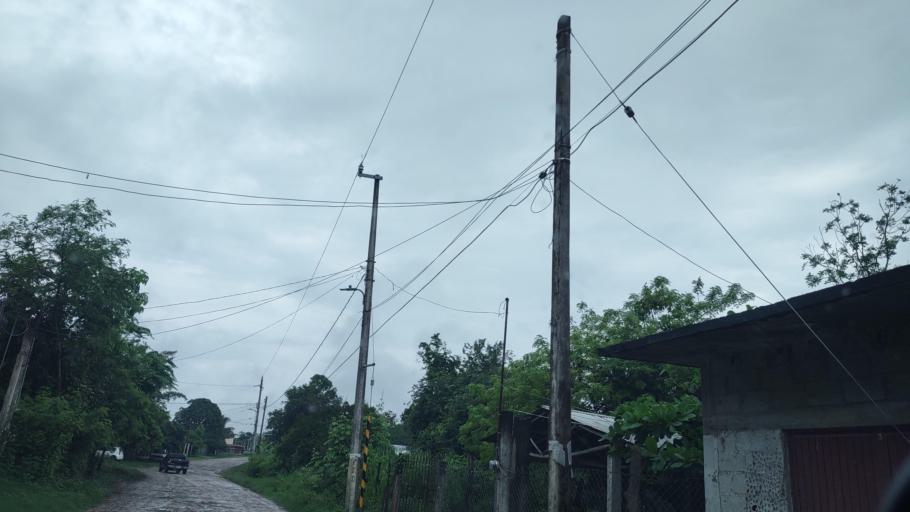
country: MX
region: San Luis Potosi
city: Tanquian de Escobedo
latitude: 21.5434
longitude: -98.5524
